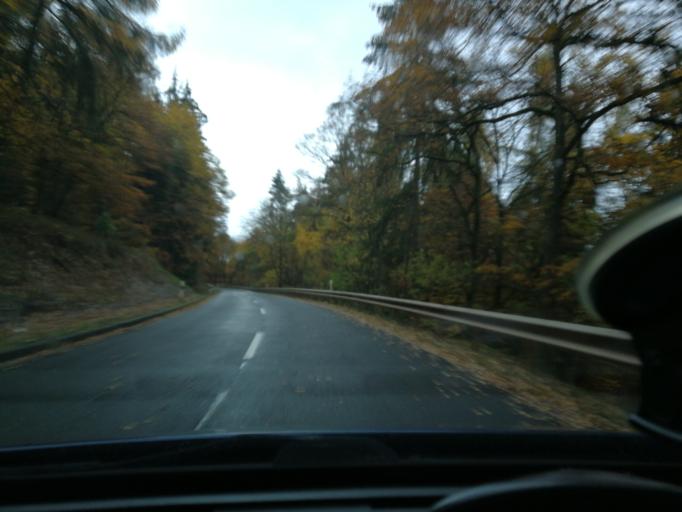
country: DE
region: Rheinland-Pfalz
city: Klausen
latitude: 49.8957
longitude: 6.8932
